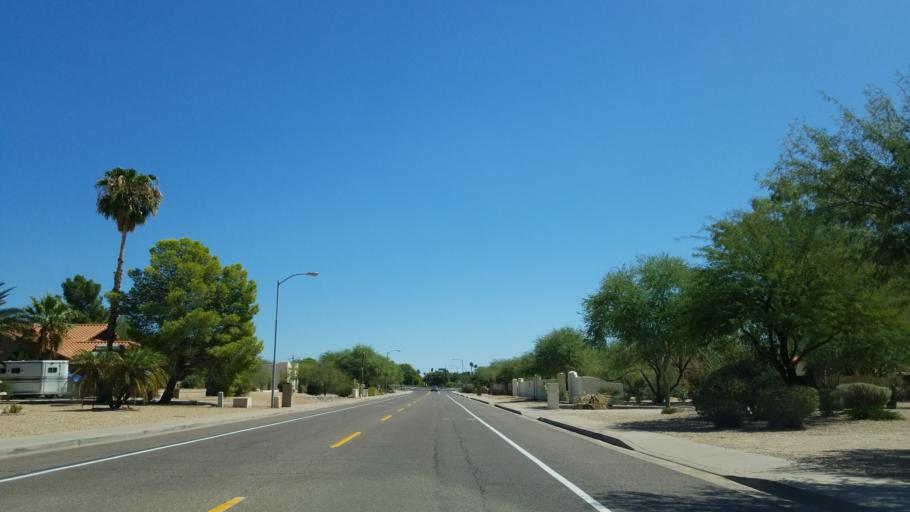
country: US
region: Arizona
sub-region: Maricopa County
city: Paradise Valley
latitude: 33.5899
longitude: -111.9806
